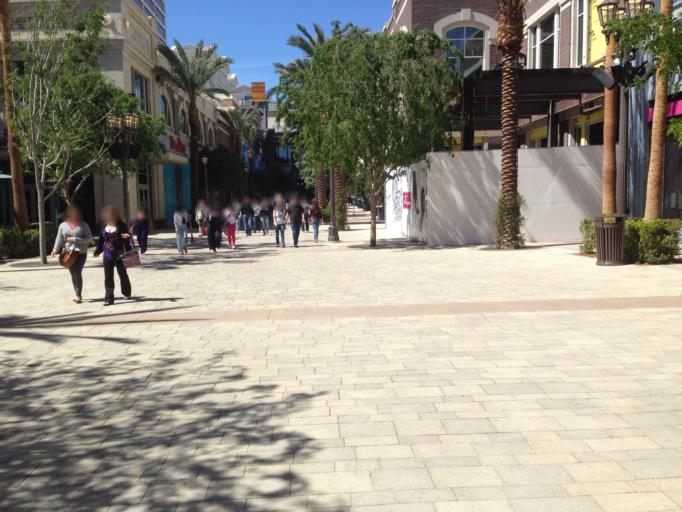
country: US
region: Nevada
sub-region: Clark County
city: Paradise
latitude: 36.1175
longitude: -115.1702
